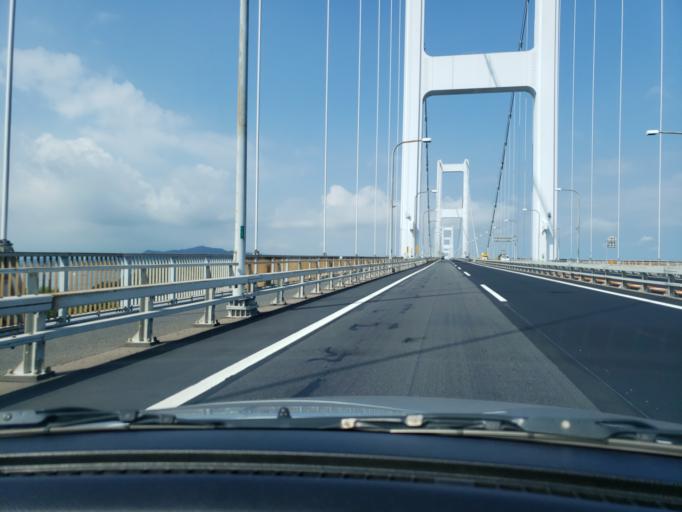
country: JP
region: Hiroshima
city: Takehara
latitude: 34.1251
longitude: 133.0107
